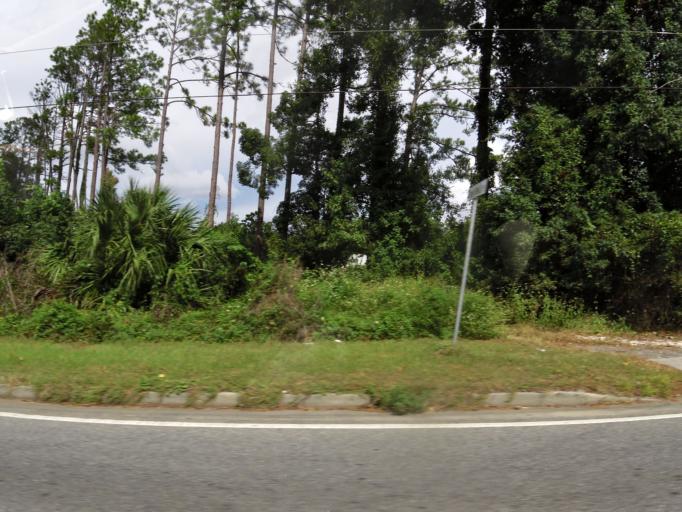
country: US
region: Georgia
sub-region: Glynn County
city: Dock Junction
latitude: 31.2126
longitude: -81.5145
